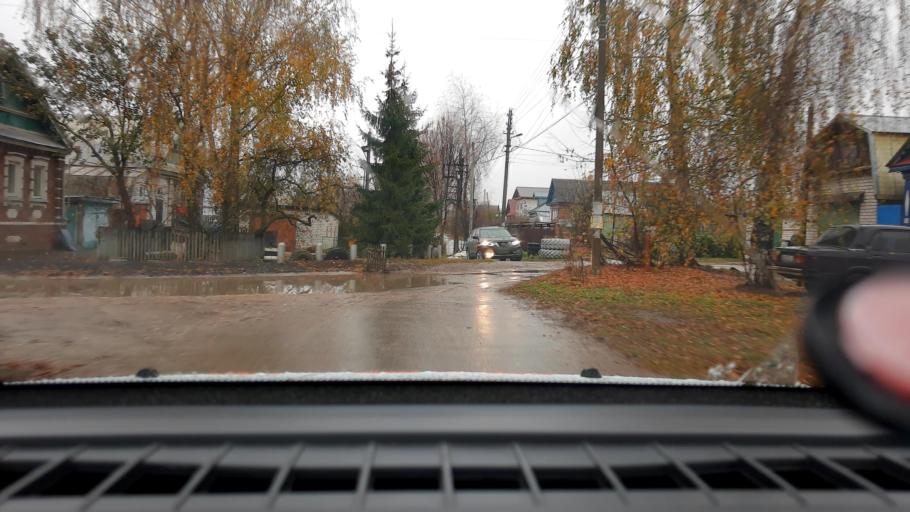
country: RU
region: Nizjnij Novgorod
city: Afonino
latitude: 56.2735
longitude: 44.1068
